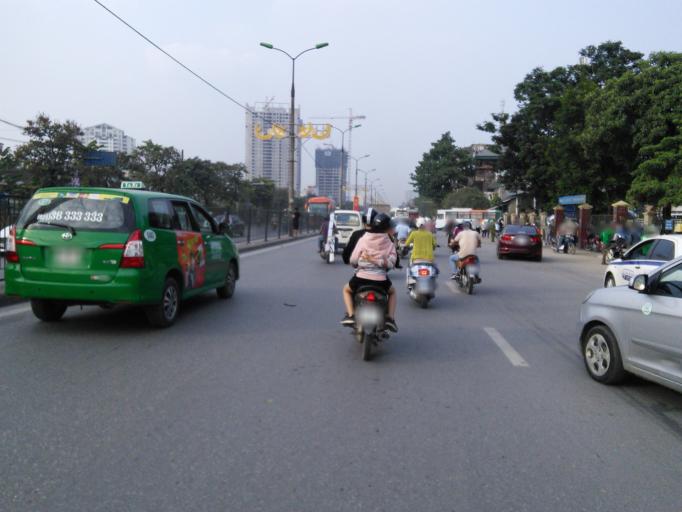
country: VN
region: Ha Noi
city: Hai BaTrung
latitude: 20.9803
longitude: 105.8410
